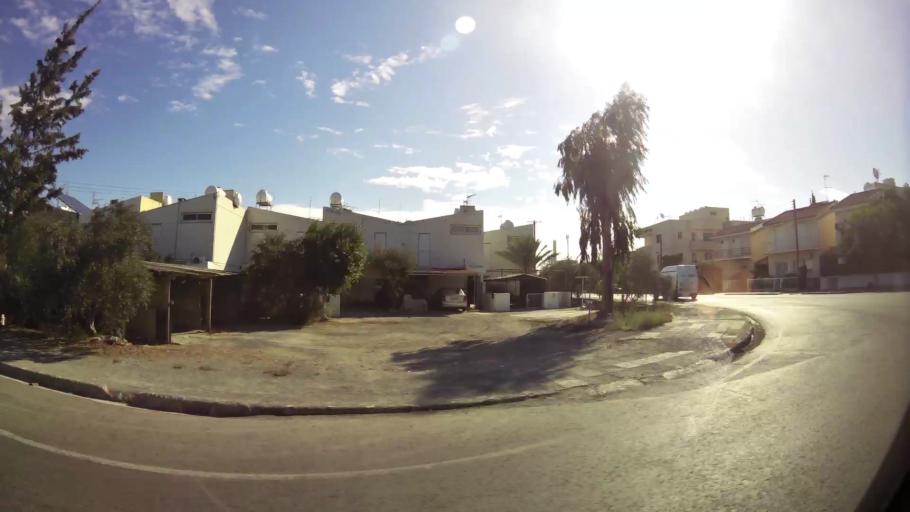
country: CY
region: Lefkosia
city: Nicosia
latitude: 35.1248
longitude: 33.3439
